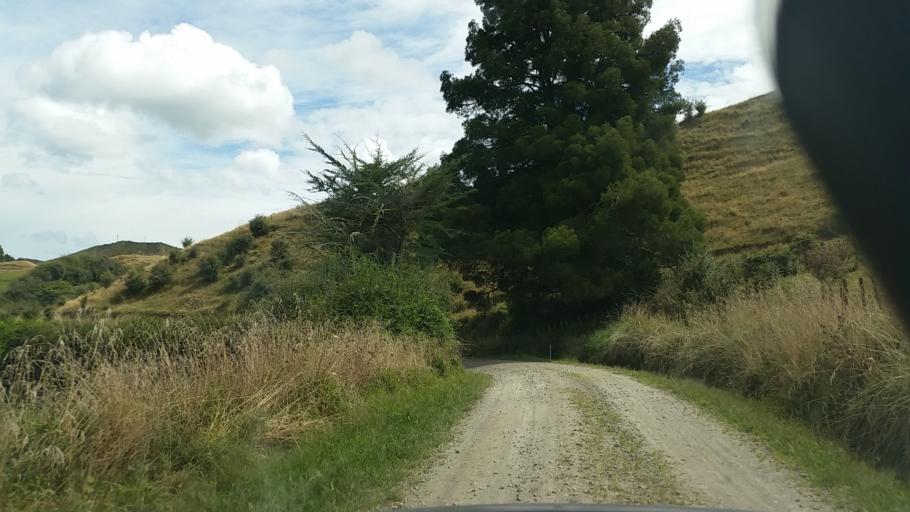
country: NZ
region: Taranaki
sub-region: South Taranaki District
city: Eltham
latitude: -39.2563
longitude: 174.5684
